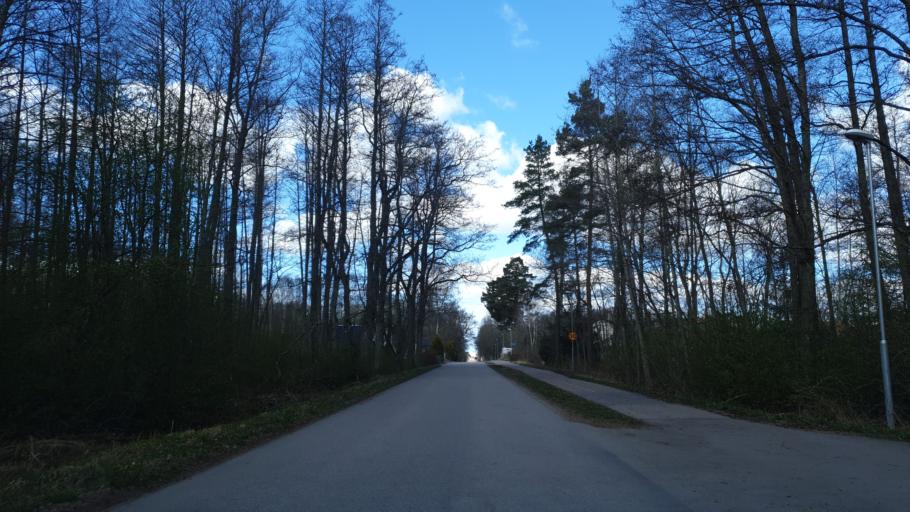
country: SE
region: Vaestmanland
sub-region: Kopings Kommun
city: Koping
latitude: 59.4838
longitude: 16.0558
